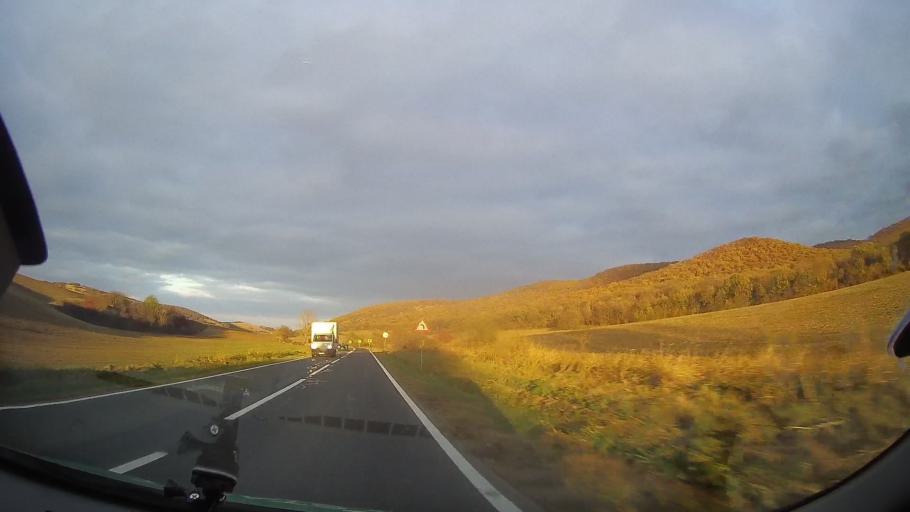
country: RO
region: Tulcea
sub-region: Comuna Ciucurova
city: Ciucurova
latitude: 44.9503
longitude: 28.5092
